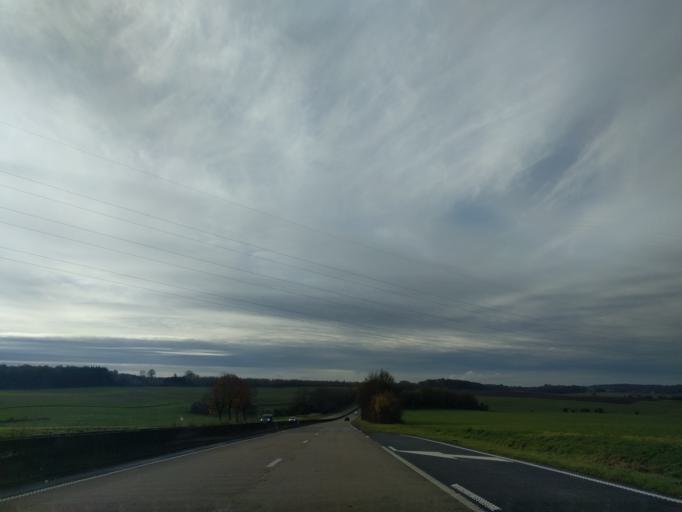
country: BE
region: Wallonia
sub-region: Province de Namur
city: Houyet
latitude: 50.2603
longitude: 5.0262
